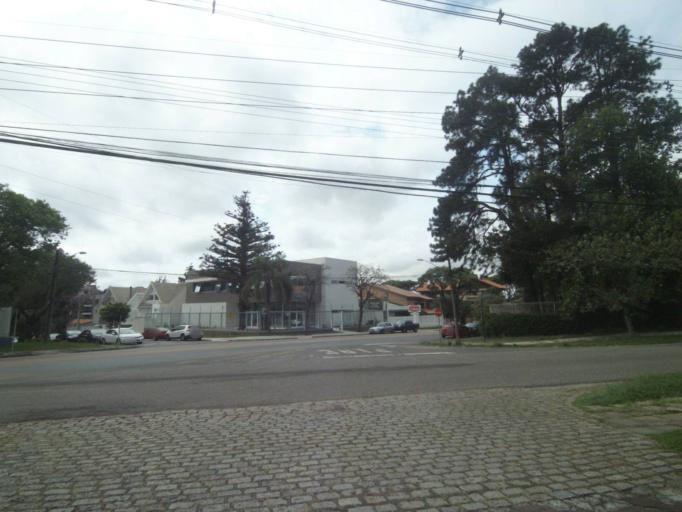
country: BR
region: Parana
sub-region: Curitiba
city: Curitiba
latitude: -25.4147
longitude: -49.2479
